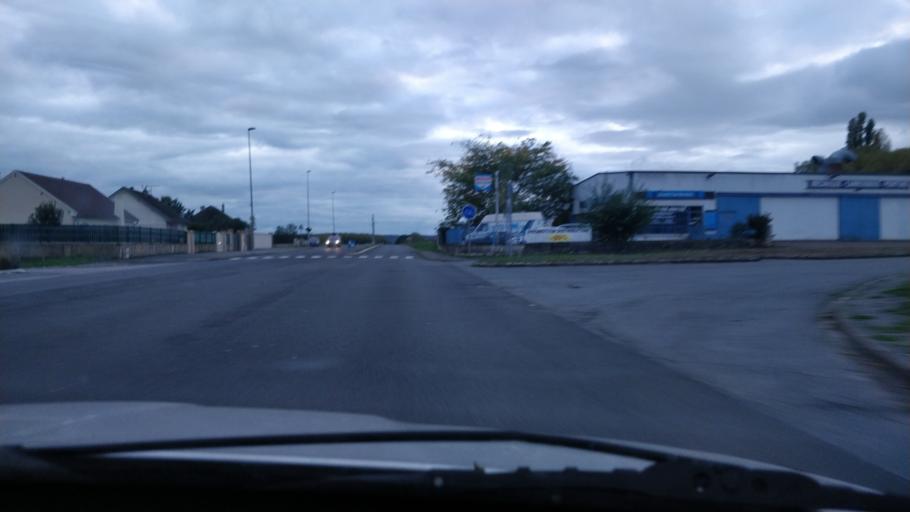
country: FR
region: Picardie
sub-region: Departement de l'Oise
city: Cambronne-les-Ribecourt
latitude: 49.4976
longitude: 2.8979
